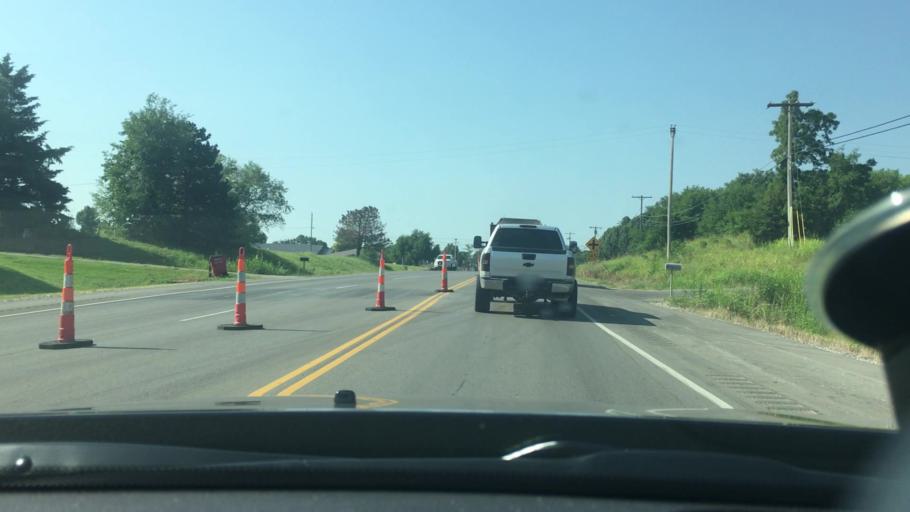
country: US
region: Oklahoma
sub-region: Garvin County
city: Lindsay
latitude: 34.8144
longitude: -97.5983
